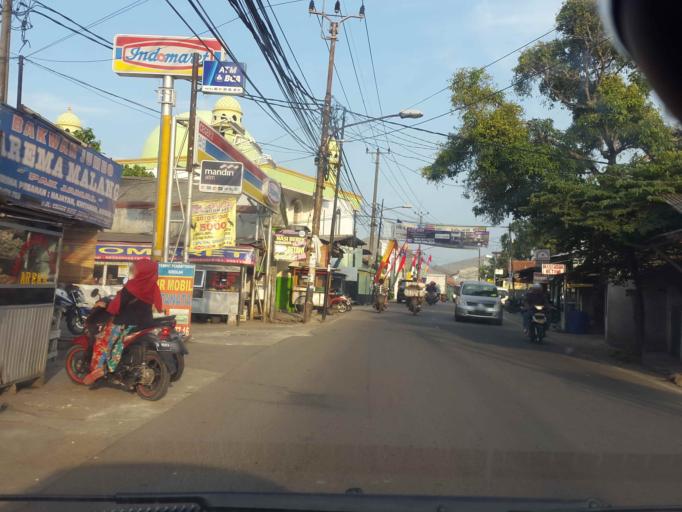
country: ID
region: Banten
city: South Tangerang
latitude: -6.2624
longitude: 106.7317
